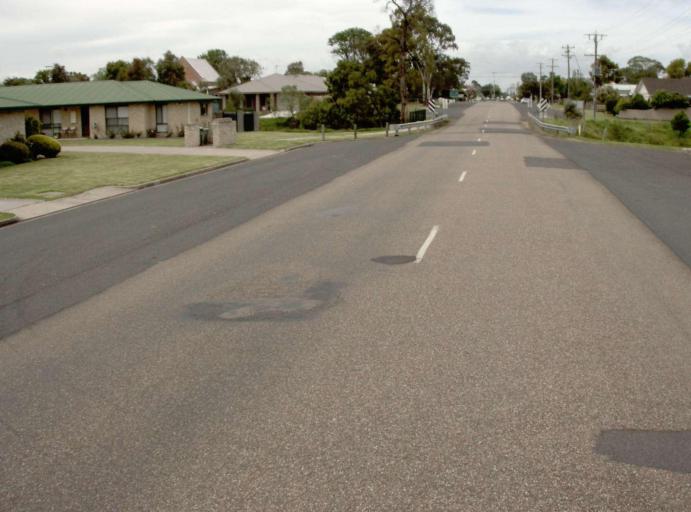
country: AU
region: Victoria
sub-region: Wellington
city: Sale
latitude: -37.9606
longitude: 147.0811
